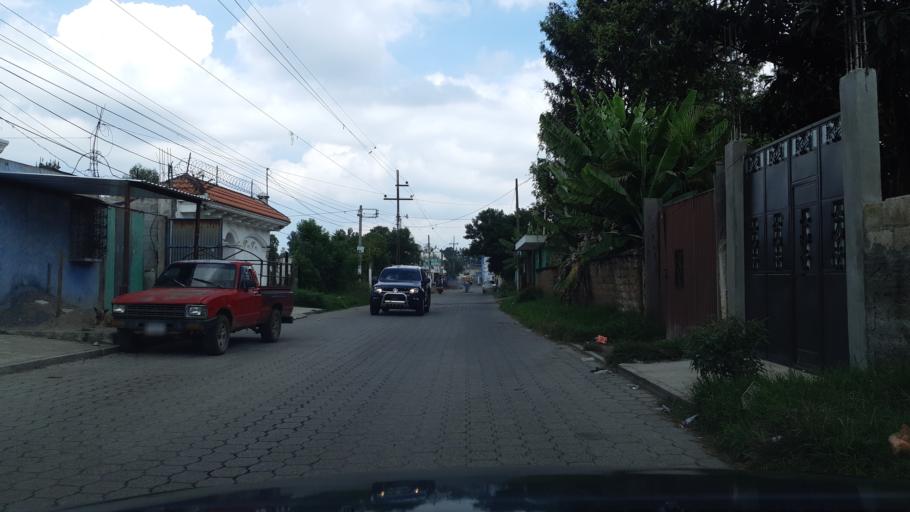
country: GT
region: Chimaltenango
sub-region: Municipio de Chimaltenango
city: Chimaltenango
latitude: 14.6708
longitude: -90.8082
